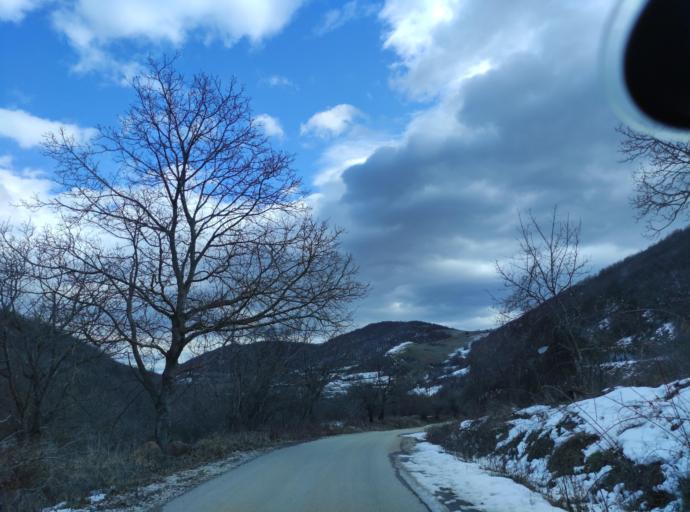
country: BG
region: Montana
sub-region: Obshtina Chiprovtsi
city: Chiprovtsi
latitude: 43.3798
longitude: 22.8634
